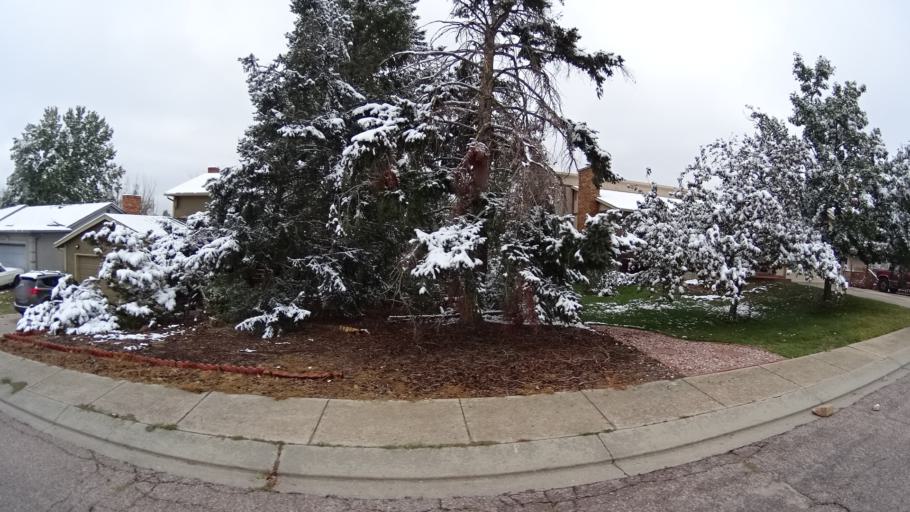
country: US
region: Colorado
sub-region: El Paso County
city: Cimarron Hills
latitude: 38.9218
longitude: -104.7729
